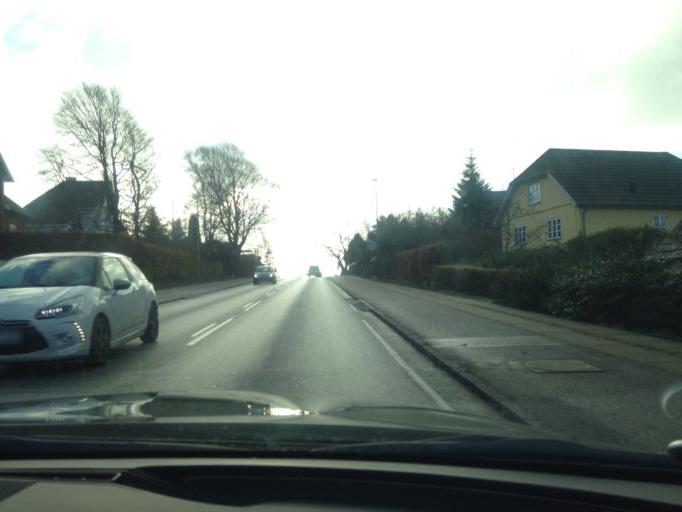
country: DK
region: South Denmark
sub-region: Kolding Kommune
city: Kolding
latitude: 55.5224
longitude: 9.4621
